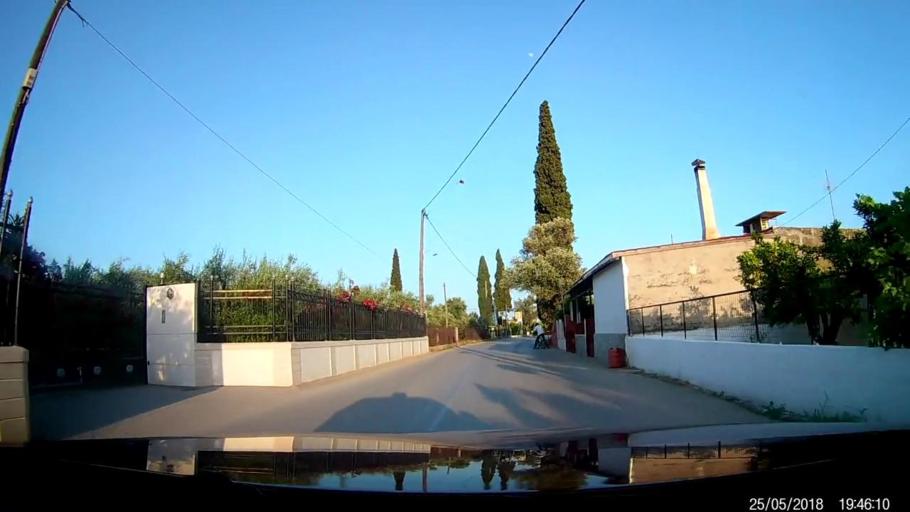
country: GR
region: Central Greece
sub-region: Nomos Evvoias
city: Ayios Nikolaos
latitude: 38.4284
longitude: 23.6389
